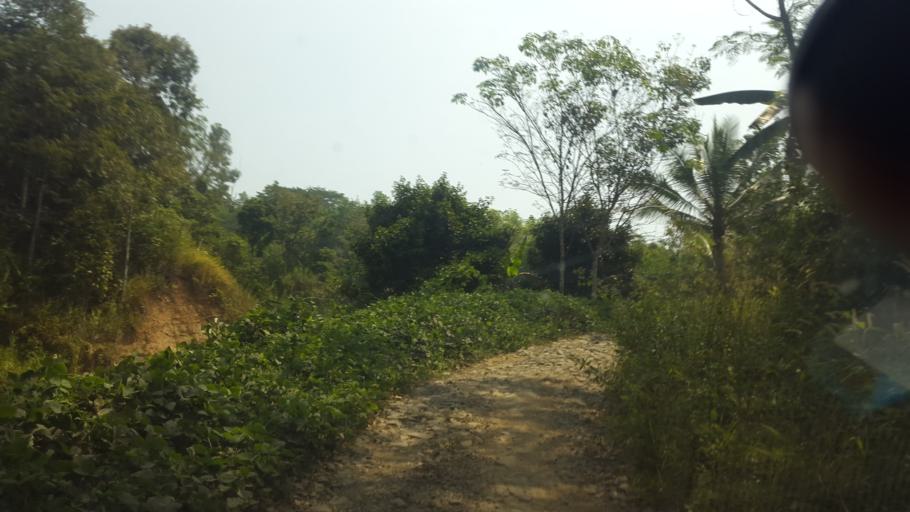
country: ID
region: West Java
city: Sindangsari
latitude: -6.9493
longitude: 106.6673
